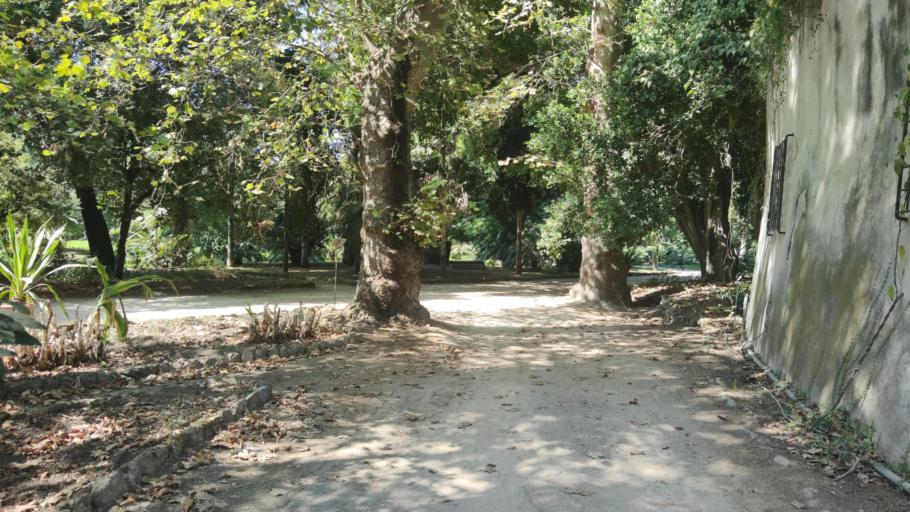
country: IT
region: Sicily
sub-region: Palermo
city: Palermo
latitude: 38.1105
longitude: 13.3748
